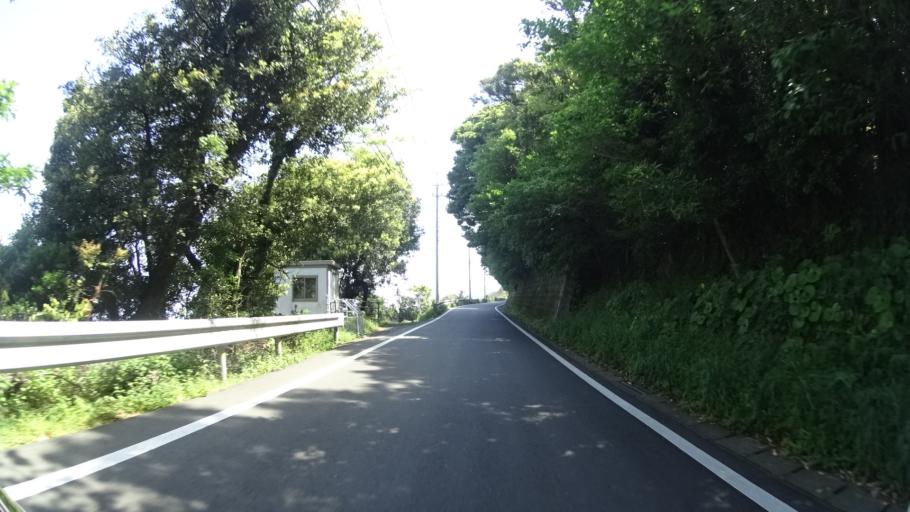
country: JP
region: Ehime
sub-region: Nishiuwa-gun
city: Ikata-cho
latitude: 33.3791
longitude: 132.0663
